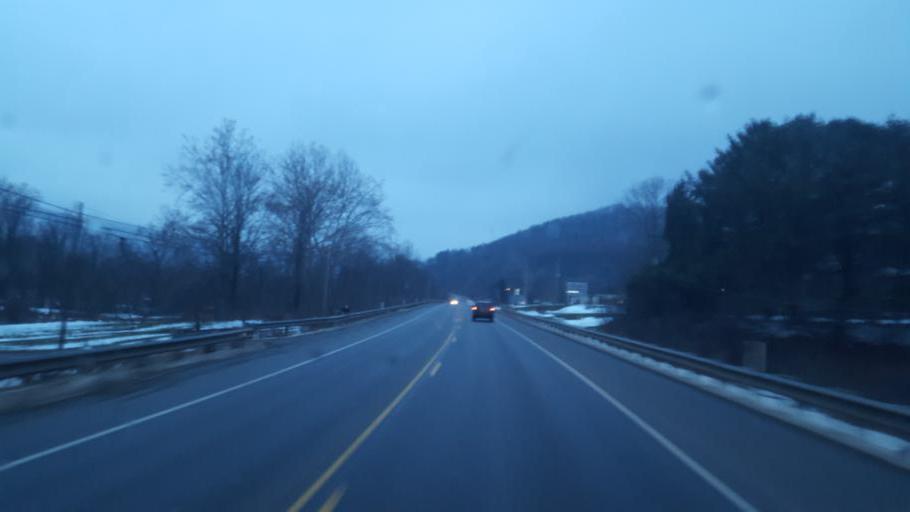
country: US
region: Pennsylvania
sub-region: McKean County
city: Port Allegany
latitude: 41.7929
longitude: -78.2150
